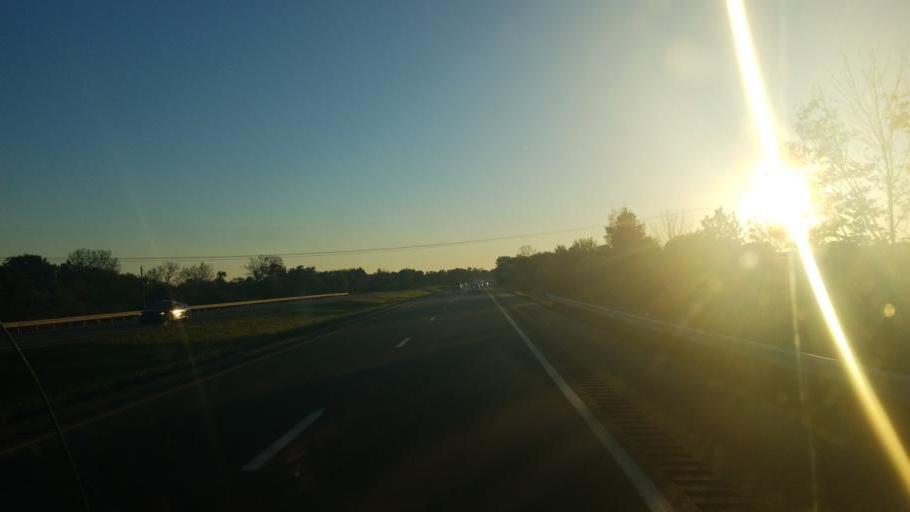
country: US
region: Ohio
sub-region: Stark County
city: Louisville
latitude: 40.8668
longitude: -81.2500
